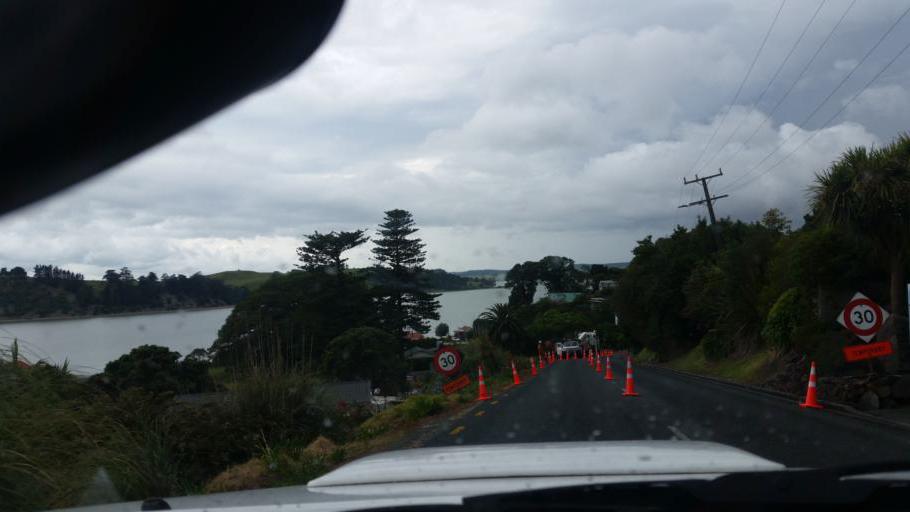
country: NZ
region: Auckland
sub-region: Auckland
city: Wellsford
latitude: -36.1558
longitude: 174.2272
